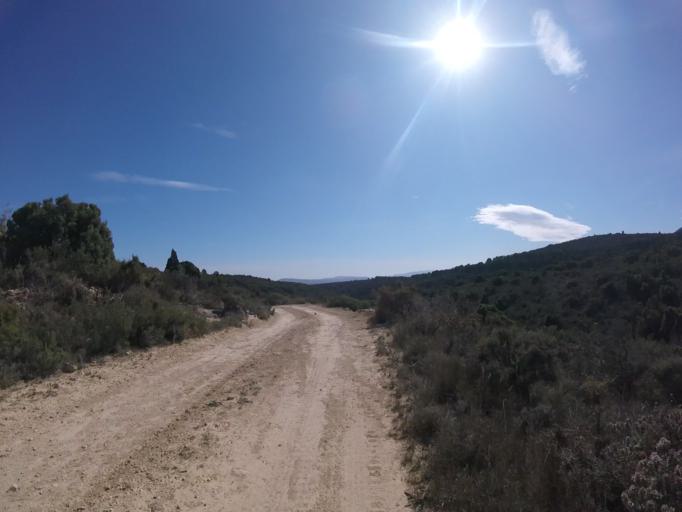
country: ES
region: Valencia
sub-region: Provincia de Castello
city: Sierra-Engarceran
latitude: 40.2727
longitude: 0.0165
